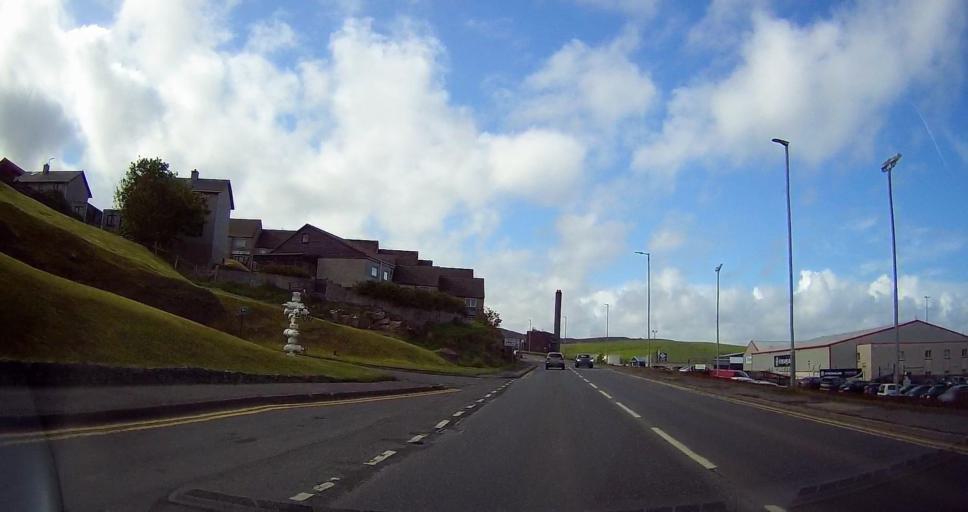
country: GB
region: Scotland
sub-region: Shetland Islands
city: Lerwick
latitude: 60.1626
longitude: -1.1594
